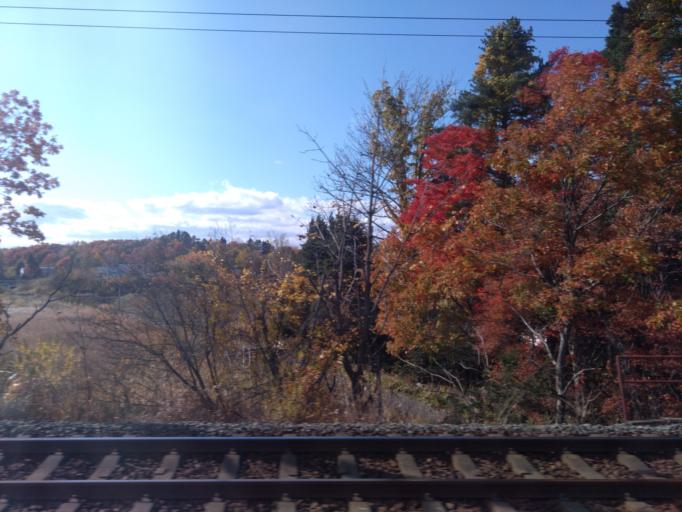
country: JP
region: Hokkaido
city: Kitahiroshima
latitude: 42.9306
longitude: 141.5726
